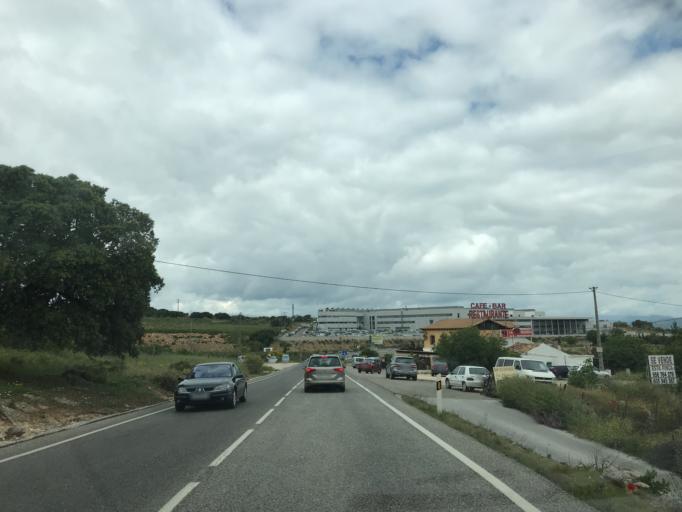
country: ES
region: Andalusia
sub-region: Provincia de Malaga
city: Ronda
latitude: 36.7202
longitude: -5.1424
